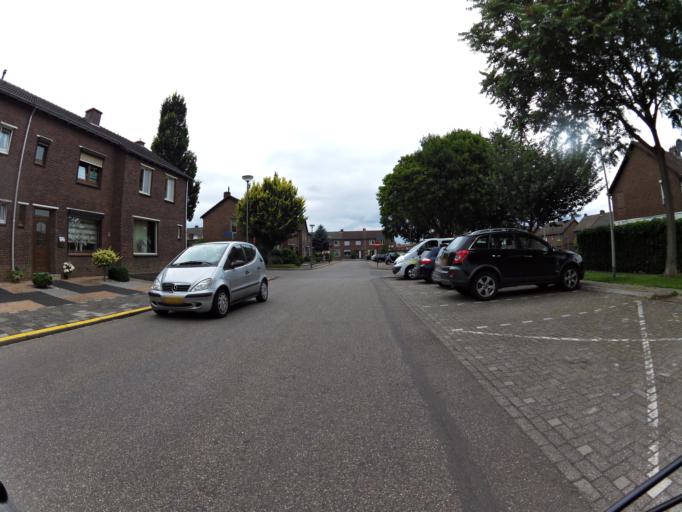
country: NL
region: Limburg
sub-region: Gemeente Kerkrade
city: Kerkrade
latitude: 50.9139
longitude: 6.0506
